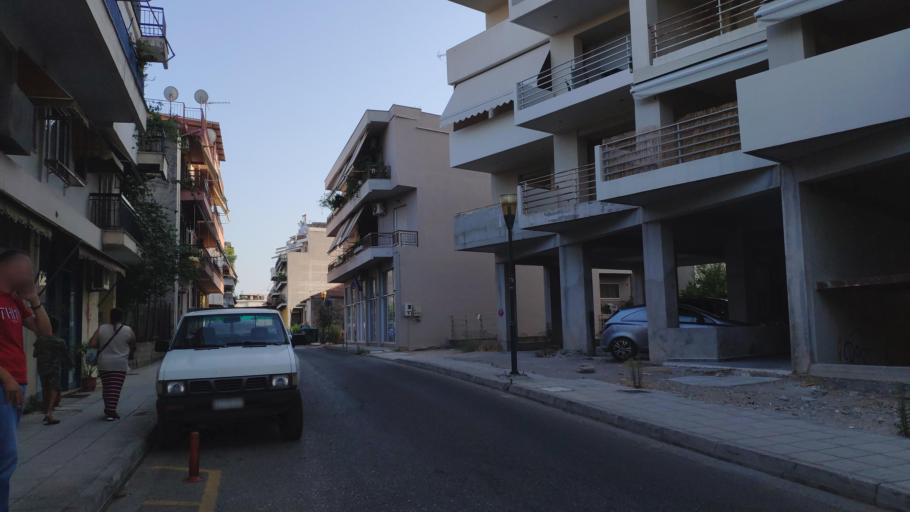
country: GR
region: West Greece
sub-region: Nomos Aitolias kai Akarnanias
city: Agrinio
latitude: 38.6203
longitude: 21.4115
